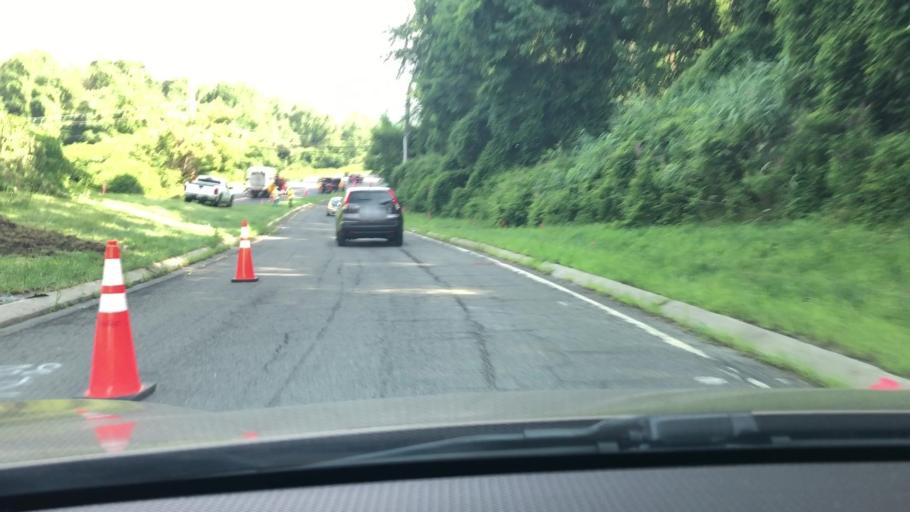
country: US
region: New York
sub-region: Westchester County
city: Elmsford
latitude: 41.0769
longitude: -73.8173
